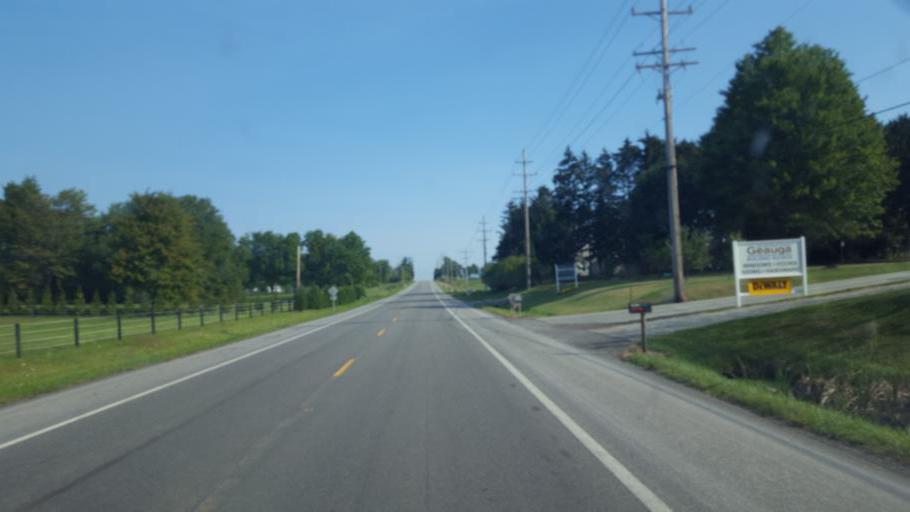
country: US
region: Ohio
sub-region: Geauga County
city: Middlefield
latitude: 41.4484
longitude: -81.0512
